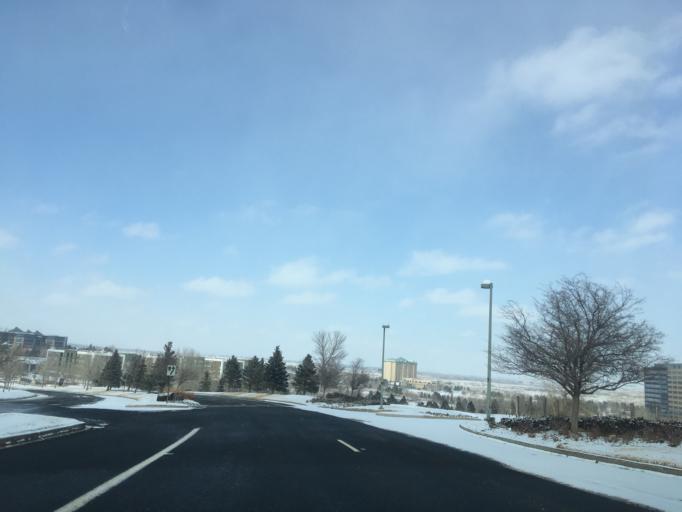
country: US
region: Colorado
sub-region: Broomfield County
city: Broomfield
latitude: 39.9192
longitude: -105.1221
